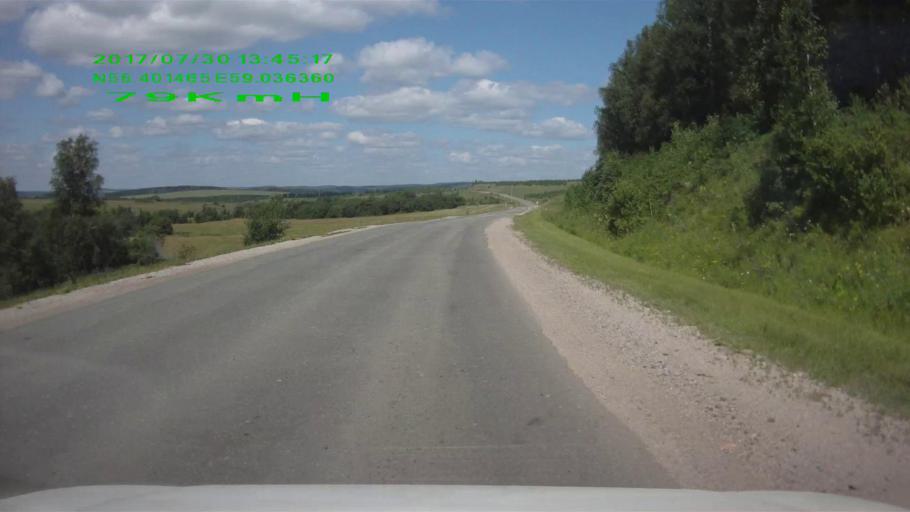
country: RU
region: Sverdlovsk
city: Mikhaylovsk
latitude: 56.4013
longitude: 59.0362
